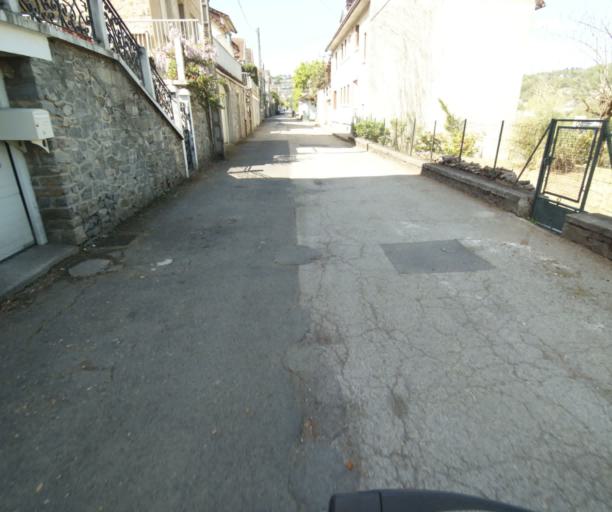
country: FR
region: Limousin
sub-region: Departement de la Correze
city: Tulle
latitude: 45.2614
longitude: 1.7611
